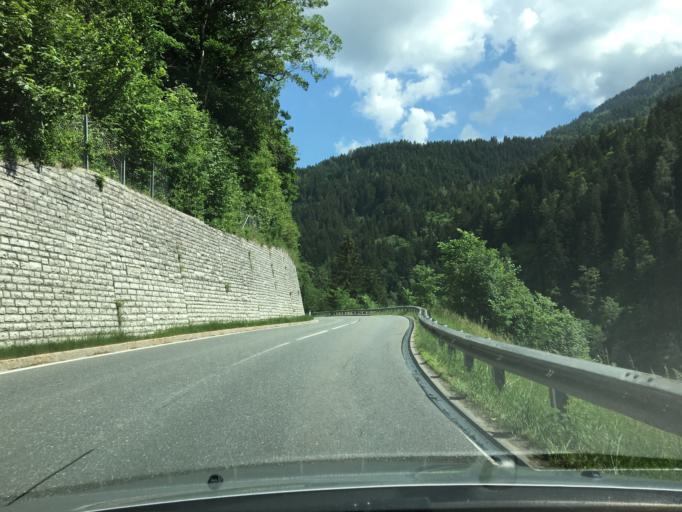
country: AT
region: Salzburg
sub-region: Politischer Bezirk Sankt Johann im Pongau
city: Sankt Johann im Pongau
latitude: 47.3323
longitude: 13.2263
